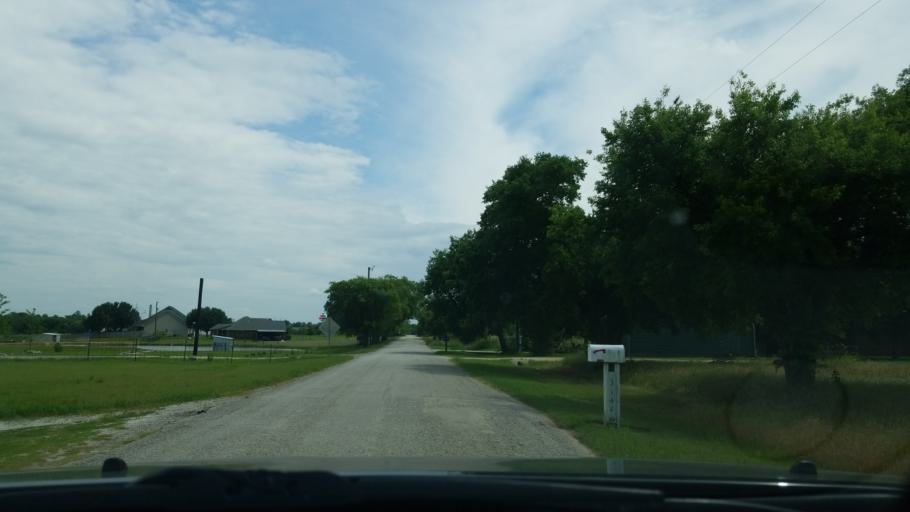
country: US
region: Texas
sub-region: Denton County
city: Sanger
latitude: 33.3073
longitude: -97.1746
